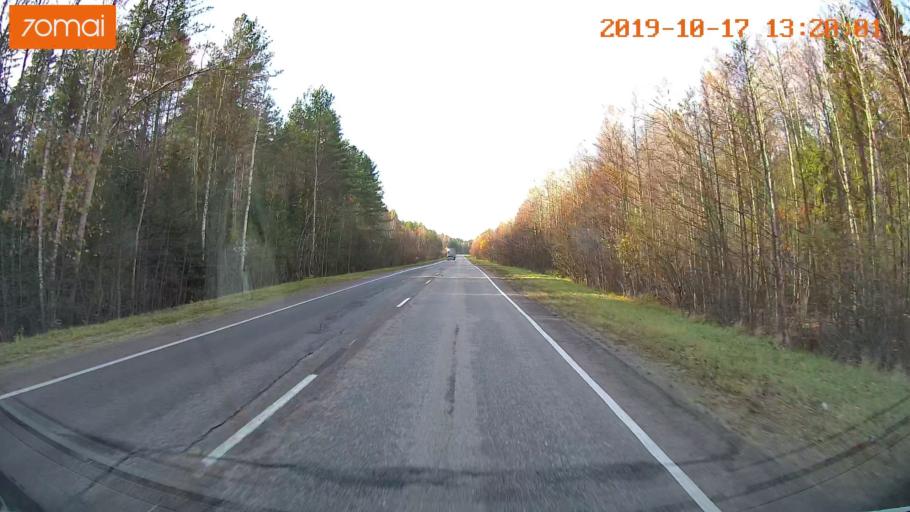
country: RU
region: Rjazan
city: Gus'-Zheleznyy
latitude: 55.0731
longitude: 41.0603
